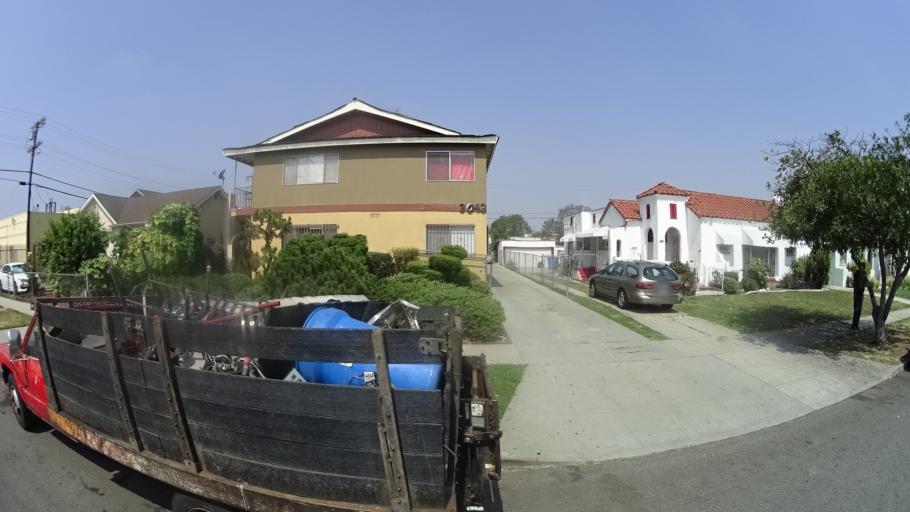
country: US
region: California
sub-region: Los Angeles County
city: View Park-Windsor Hills
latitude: 34.0264
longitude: -118.3329
